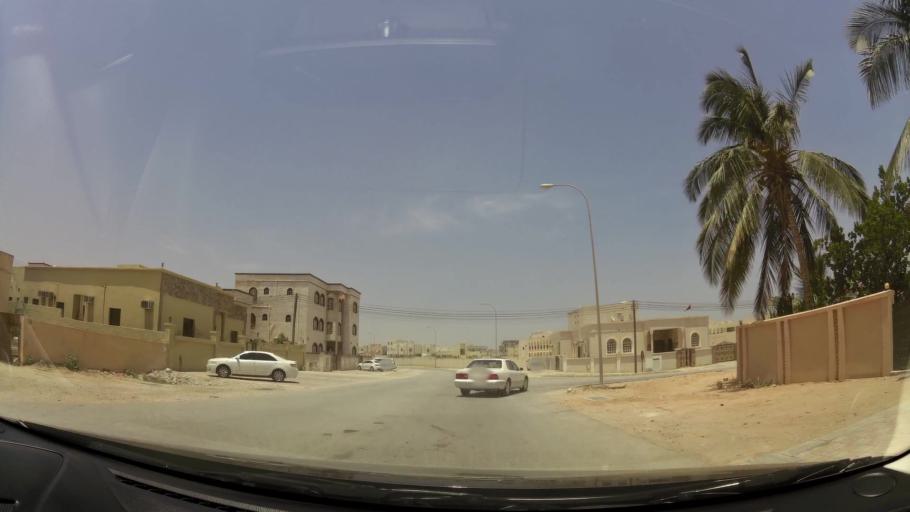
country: OM
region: Zufar
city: Salalah
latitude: 17.0694
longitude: 54.1539
